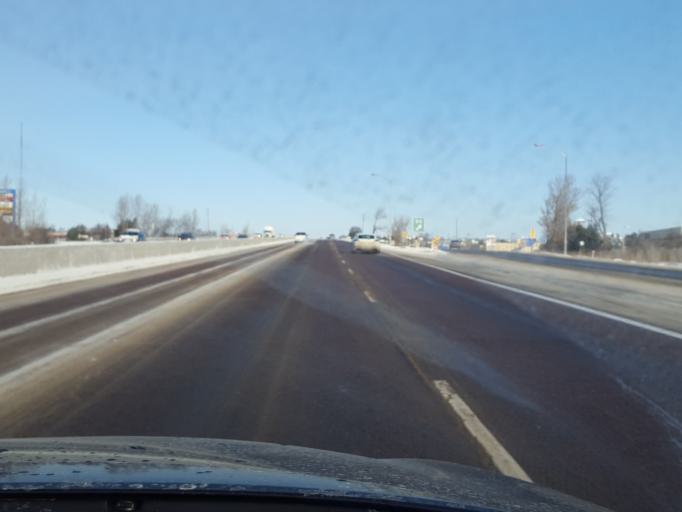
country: CA
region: Ontario
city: Innisfil
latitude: 44.3314
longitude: -79.6837
